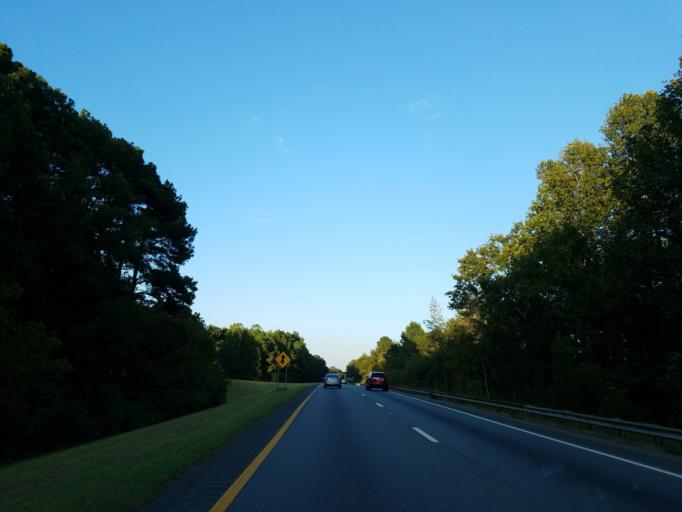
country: US
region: North Carolina
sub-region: Cleveland County
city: White Plains
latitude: 35.1944
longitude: -81.3928
